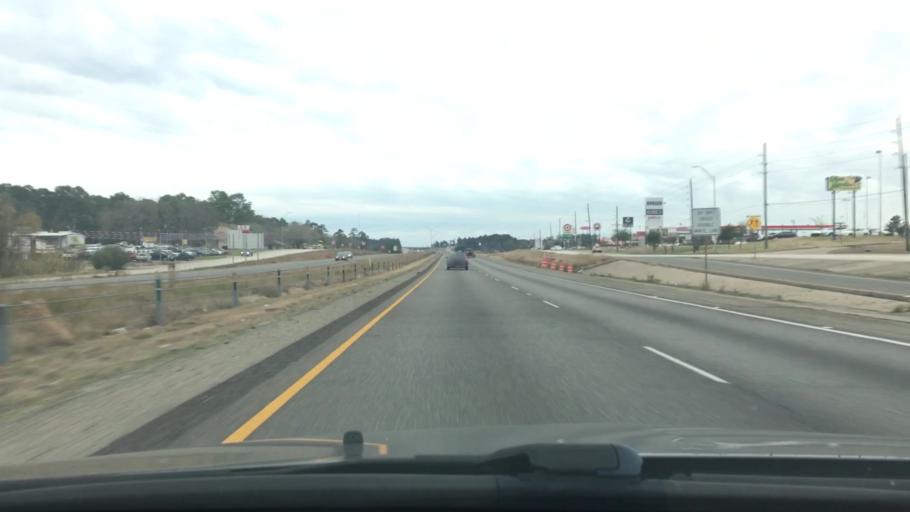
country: US
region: Texas
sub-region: Walker County
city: Huntsville
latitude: 30.7116
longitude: -95.5655
